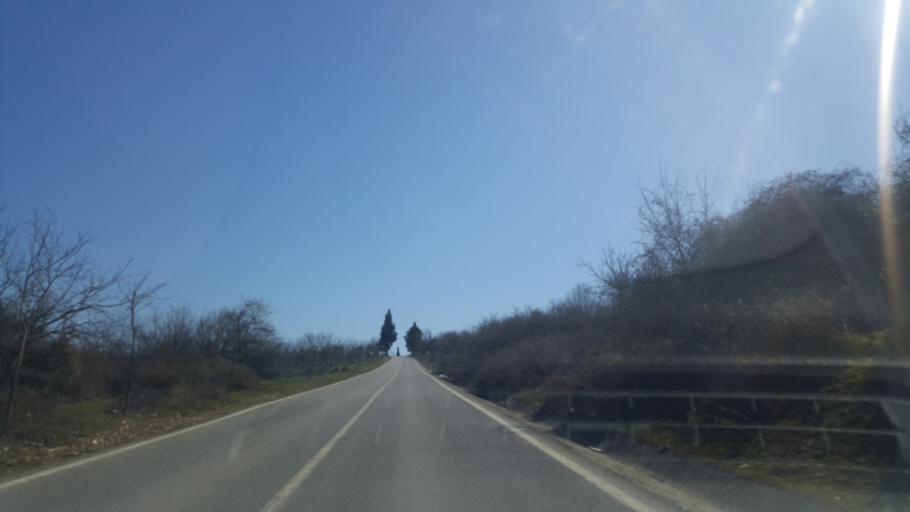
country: TR
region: Kocaeli
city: Tavsancil
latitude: 40.7871
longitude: 29.5723
